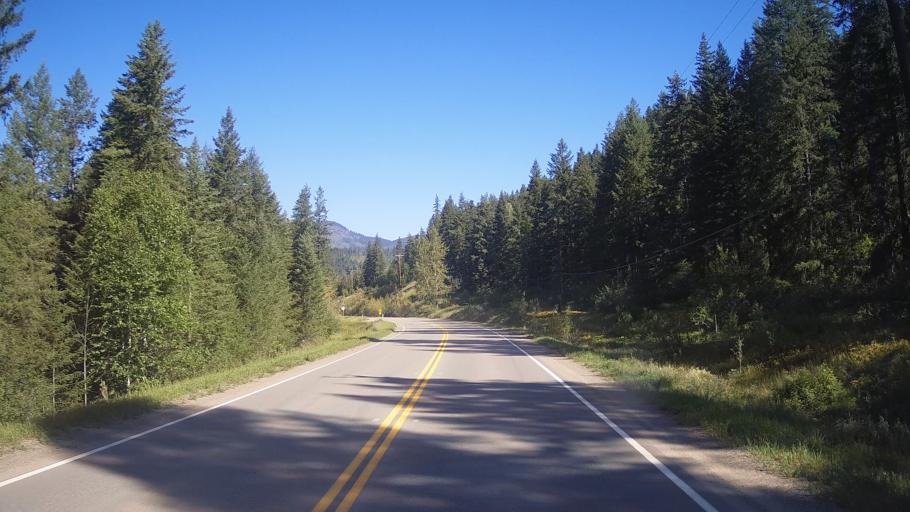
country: CA
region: British Columbia
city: Kamloops
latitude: 51.4499
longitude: -120.2137
